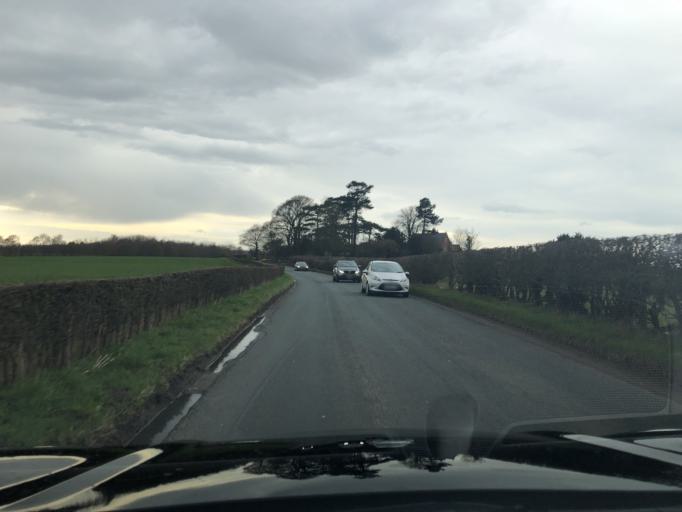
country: GB
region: England
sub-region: North Yorkshire
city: Northallerton
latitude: 54.3430
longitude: -1.4593
